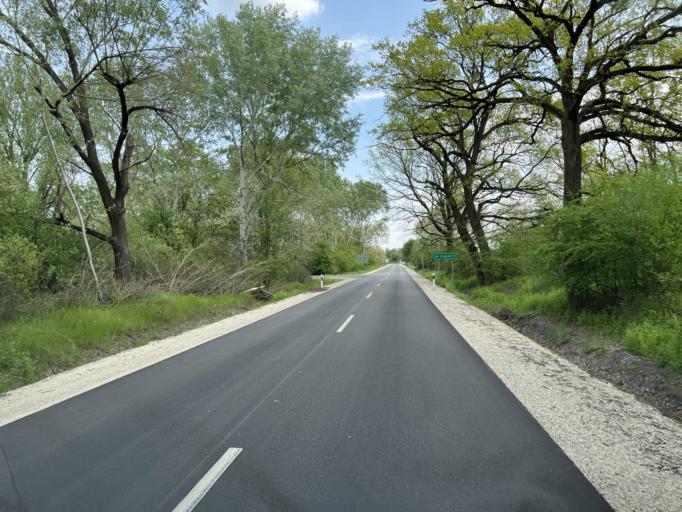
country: HU
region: Pest
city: Csemo
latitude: 47.0825
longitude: 19.6679
